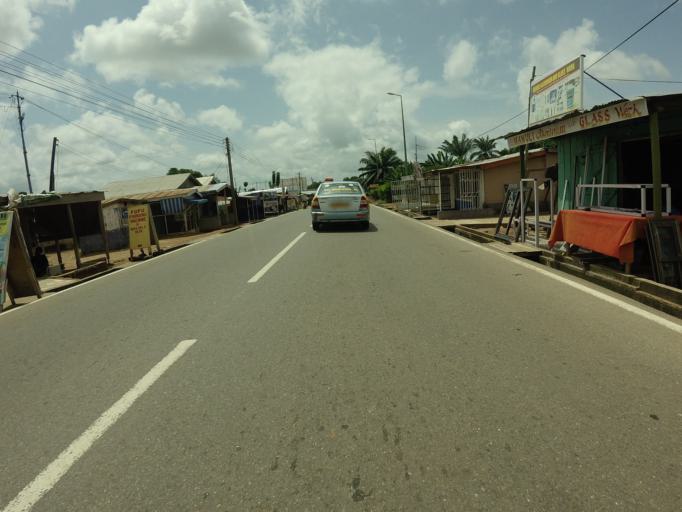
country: GH
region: Volta
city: Ho
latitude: 6.6043
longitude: 0.4730
